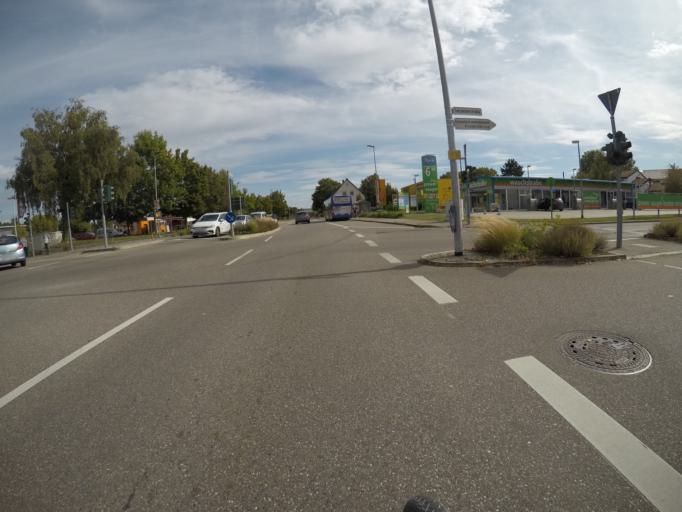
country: DE
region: Baden-Wuerttemberg
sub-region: Regierungsbezirk Stuttgart
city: Vaihingen an der Enz
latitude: 48.9271
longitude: 8.9654
